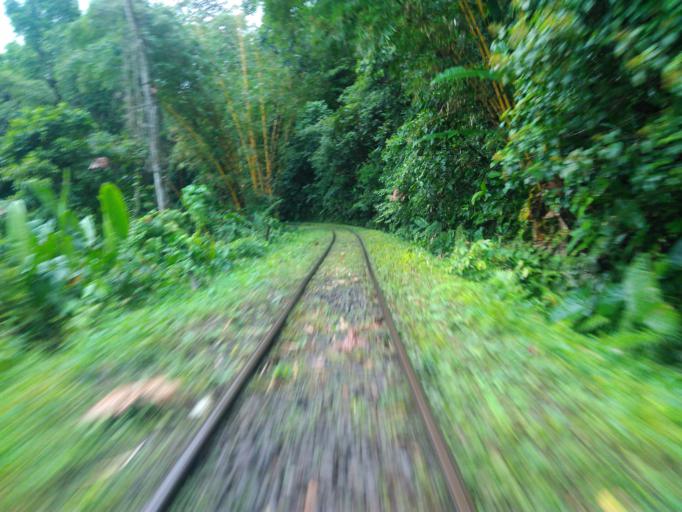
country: CO
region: Valle del Cauca
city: Buenaventura
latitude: 3.8463
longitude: -76.8869
